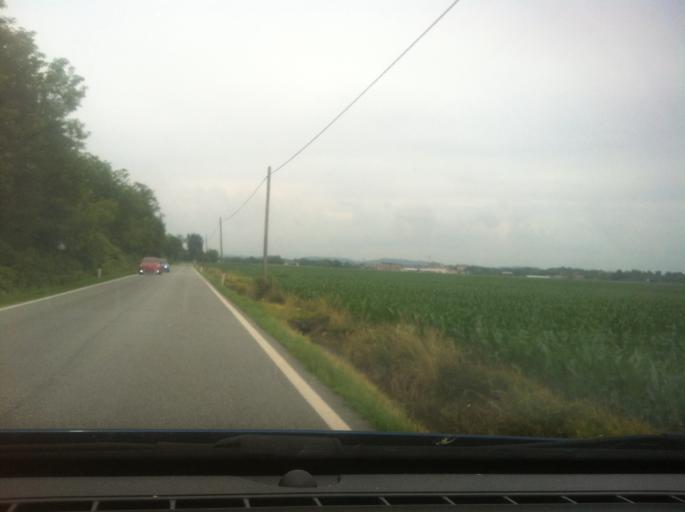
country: IT
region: Piedmont
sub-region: Provincia di Torino
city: Foglizzo
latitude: 45.2540
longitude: 7.8102
